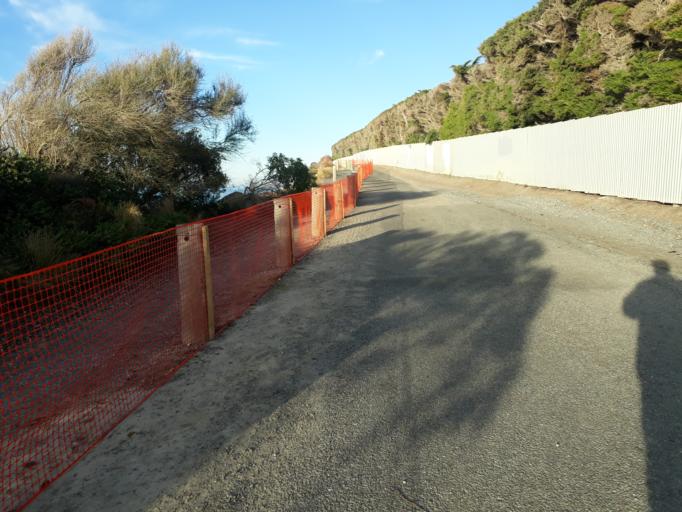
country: NZ
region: Canterbury
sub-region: Timaru District
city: Timaru
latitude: -44.4132
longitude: 171.2648
